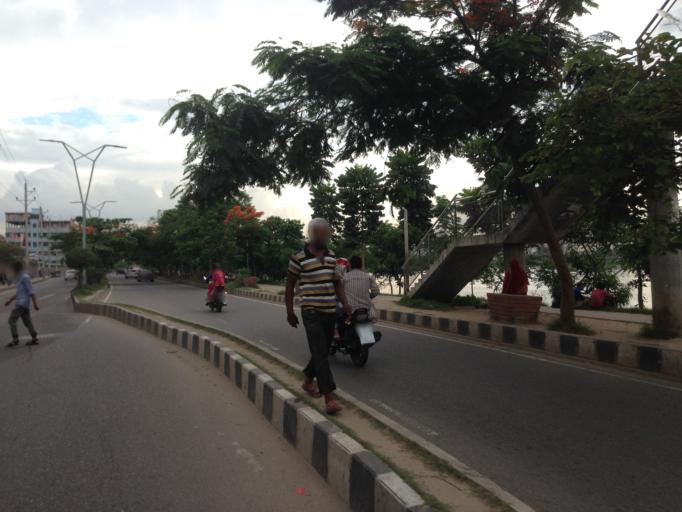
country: BD
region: Dhaka
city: Paltan
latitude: 23.7681
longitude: 90.4217
